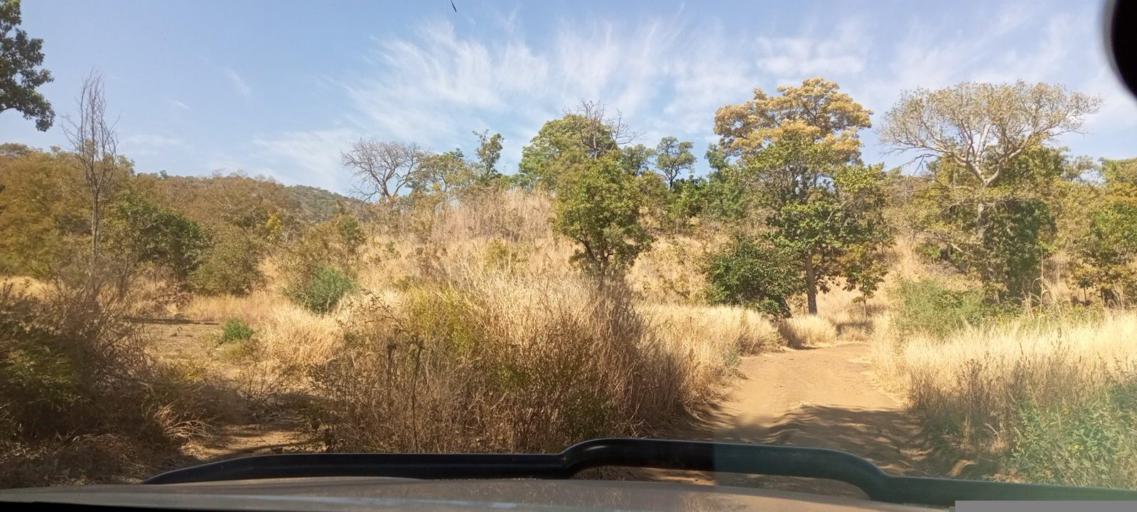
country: ML
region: Koulikoro
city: Kangaba
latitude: 12.3011
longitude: -8.6545
